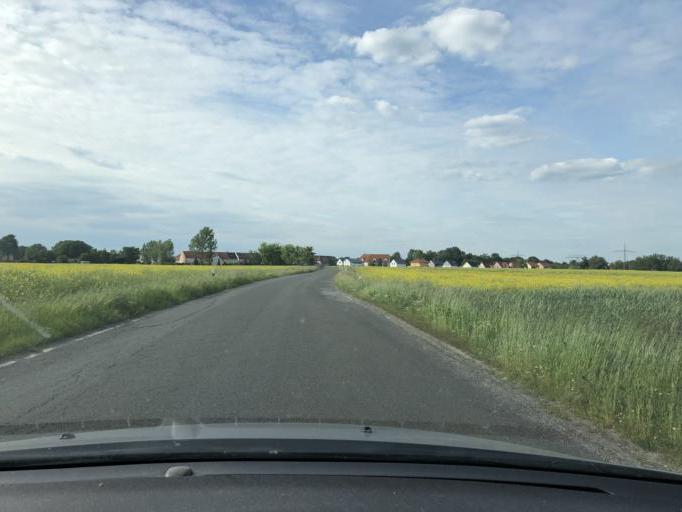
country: DE
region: Saxony
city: Borsdorf
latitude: 51.3355
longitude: 12.5259
